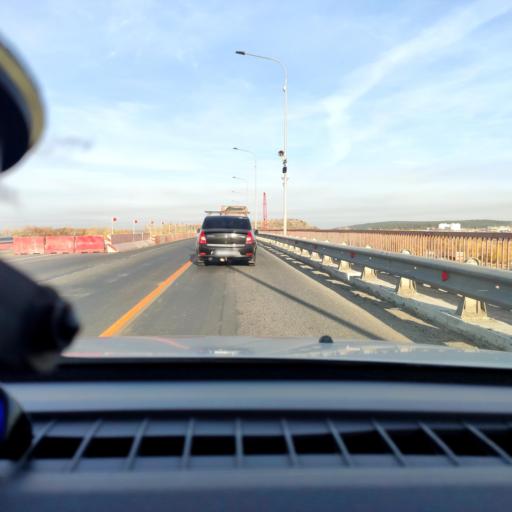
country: RU
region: Samara
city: Volzhskiy
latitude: 53.4112
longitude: 50.1385
